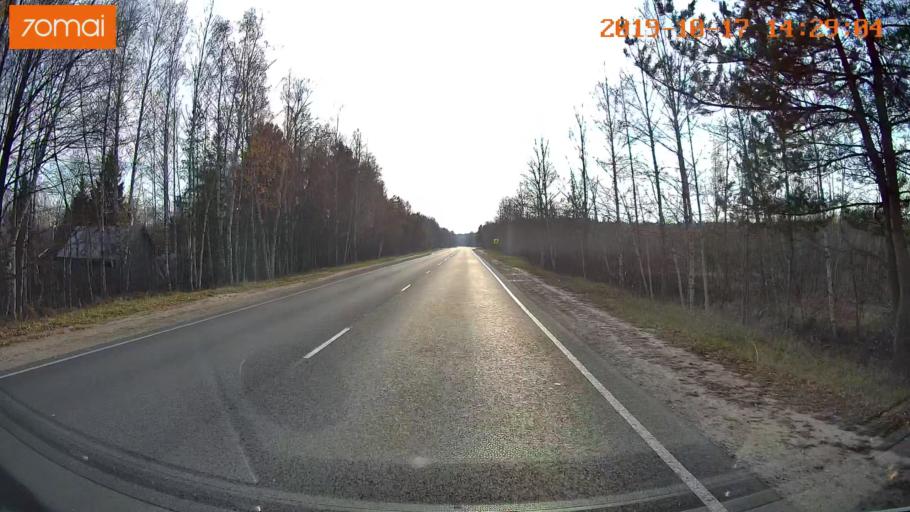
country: RU
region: Rjazan
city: Solotcha
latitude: 54.9652
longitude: 39.9464
